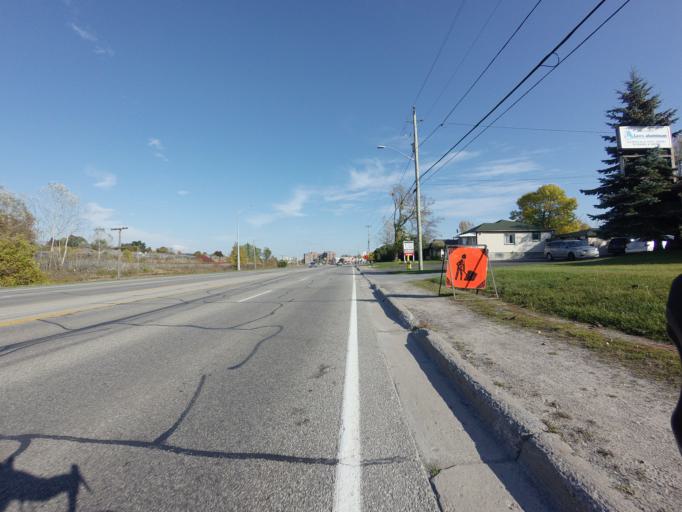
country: CA
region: Ontario
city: Kingston
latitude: 44.2374
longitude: -76.5873
